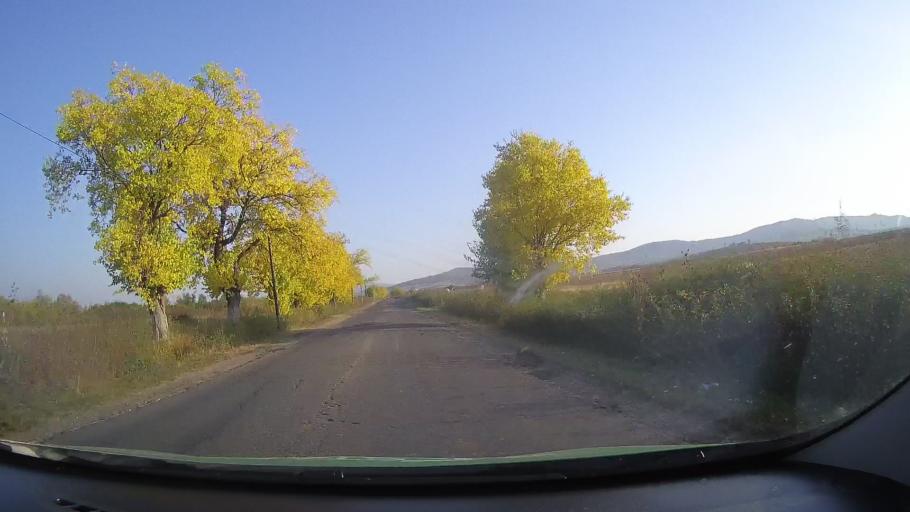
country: RO
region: Arad
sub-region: Comuna Pancota
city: Pancota
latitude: 46.3141
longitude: 21.7018
